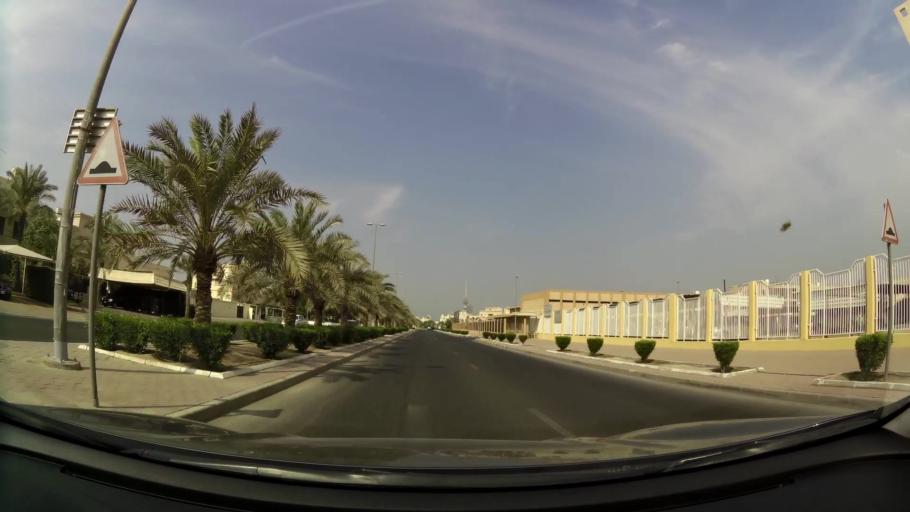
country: KW
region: Al Asimah
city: Ash Shamiyah
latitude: 29.3376
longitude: 47.9766
